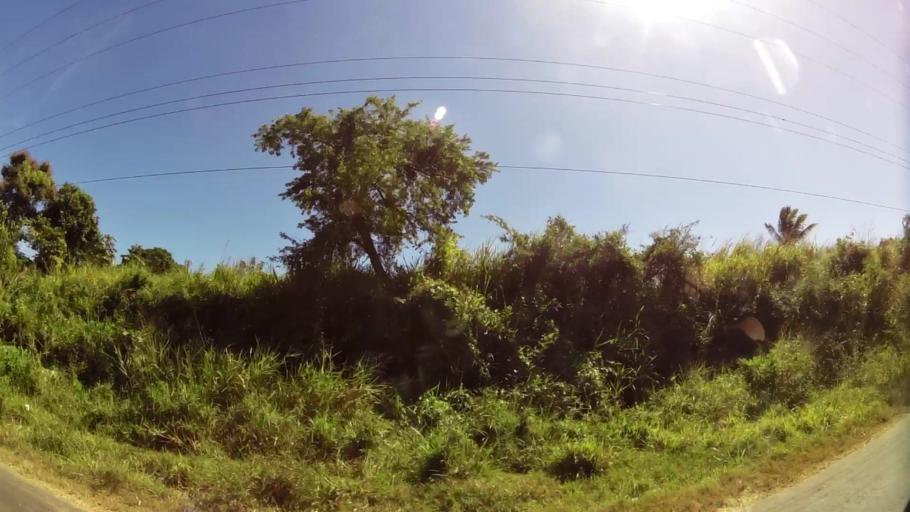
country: SV
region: Ahuachapan
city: Ahuachapan
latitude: 13.9343
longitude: -89.8402
